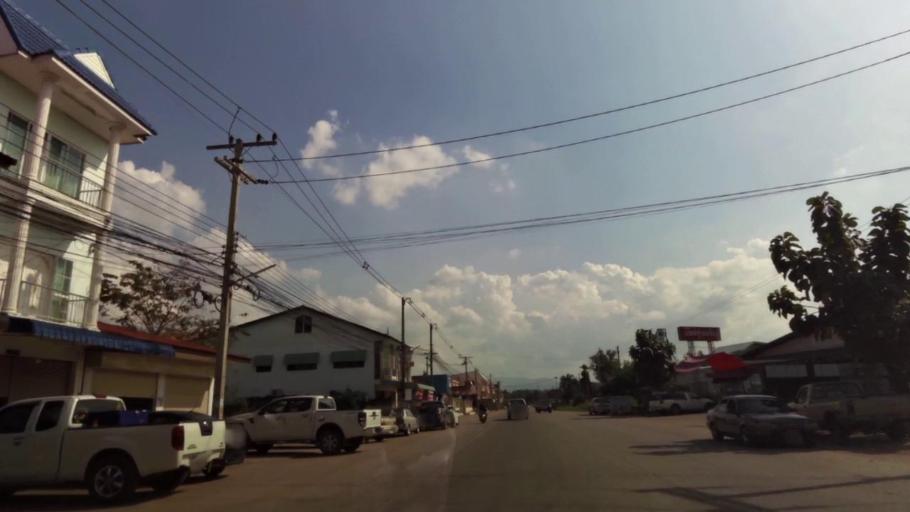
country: TH
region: Phrae
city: Phrae
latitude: 18.1219
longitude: 100.1537
